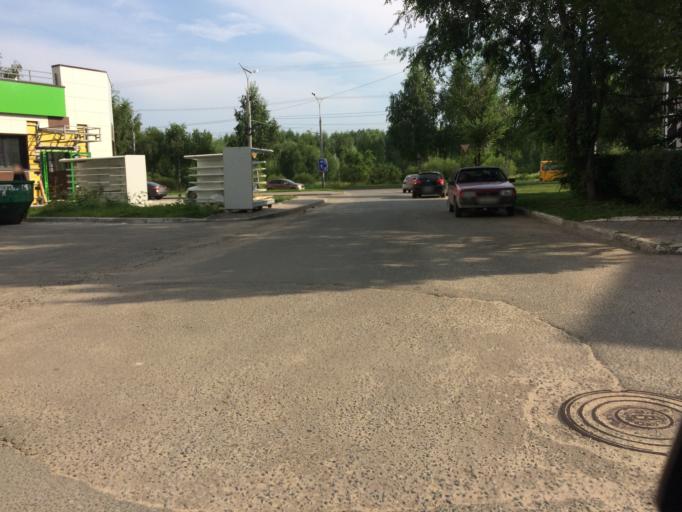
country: RU
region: Mariy-El
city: Yoshkar-Ola
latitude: 56.6274
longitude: 47.9108
